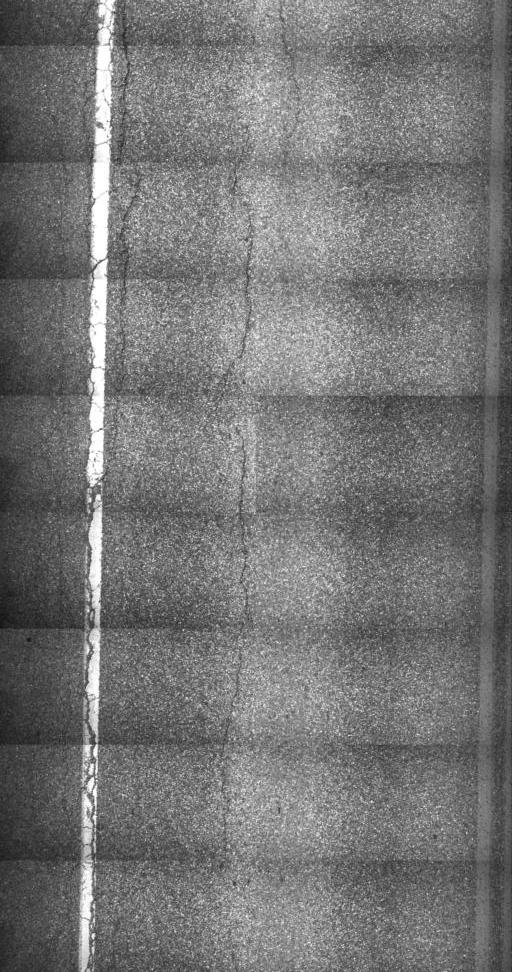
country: US
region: Vermont
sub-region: Bennington County
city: Manchester Center
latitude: 43.2075
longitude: -73.0623
